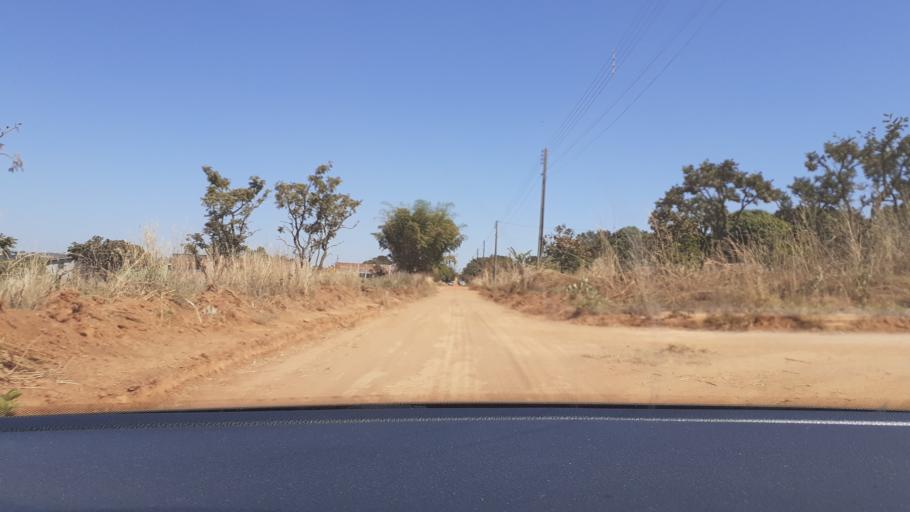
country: BR
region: Goias
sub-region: Aparecida De Goiania
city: Aparecida de Goiania
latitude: -16.8715
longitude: -49.2766
